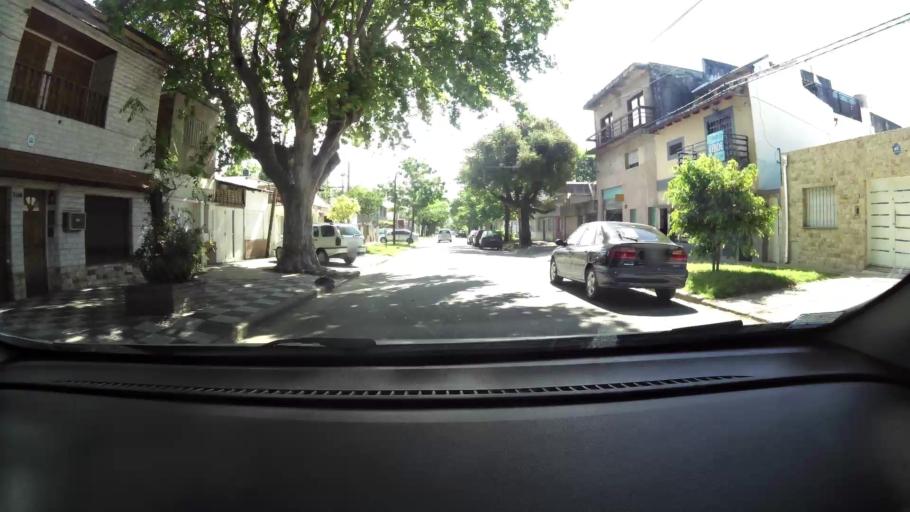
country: AR
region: Santa Fe
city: Granadero Baigorria
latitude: -32.9336
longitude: -60.7182
